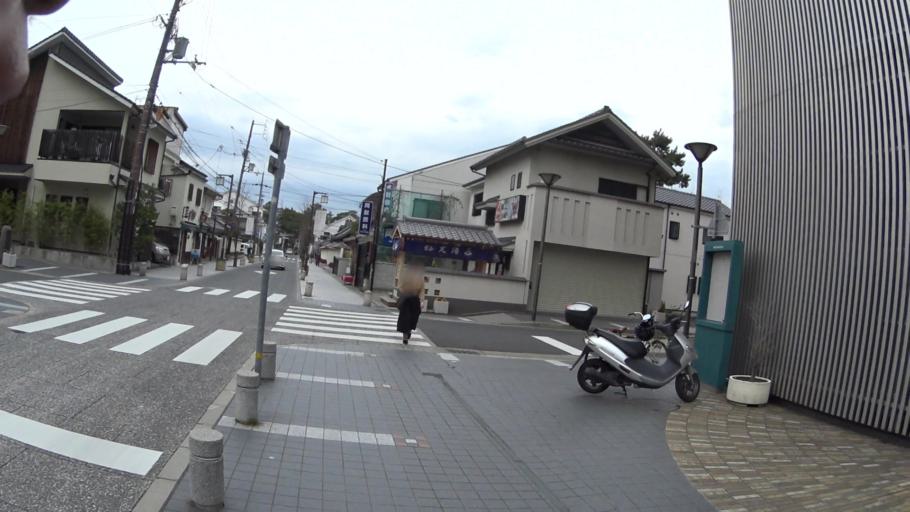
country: JP
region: Hyogo
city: Itami
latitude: 34.7842
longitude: 135.4152
